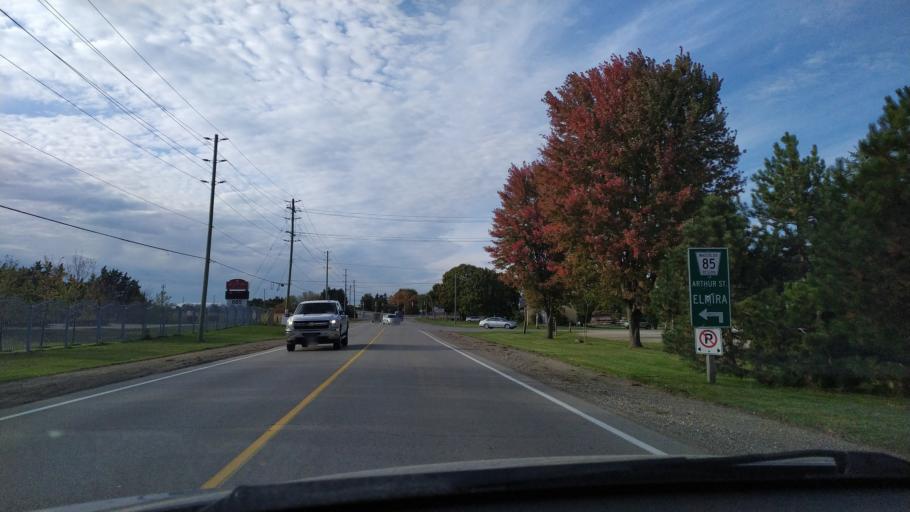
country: CA
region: Ontario
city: Waterloo
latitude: 43.5089
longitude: -80.5415
